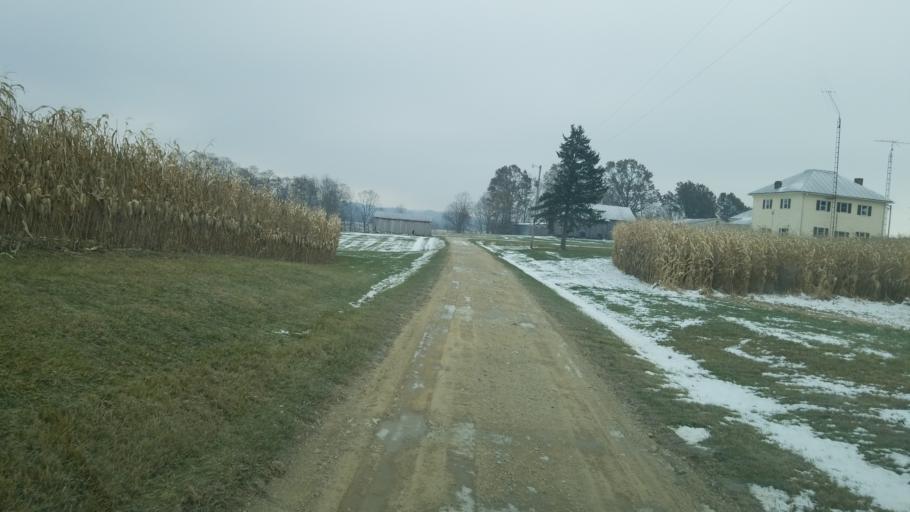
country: US
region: Ohio
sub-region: Richland County
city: Lexington
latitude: 40.5901
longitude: -82.6036
